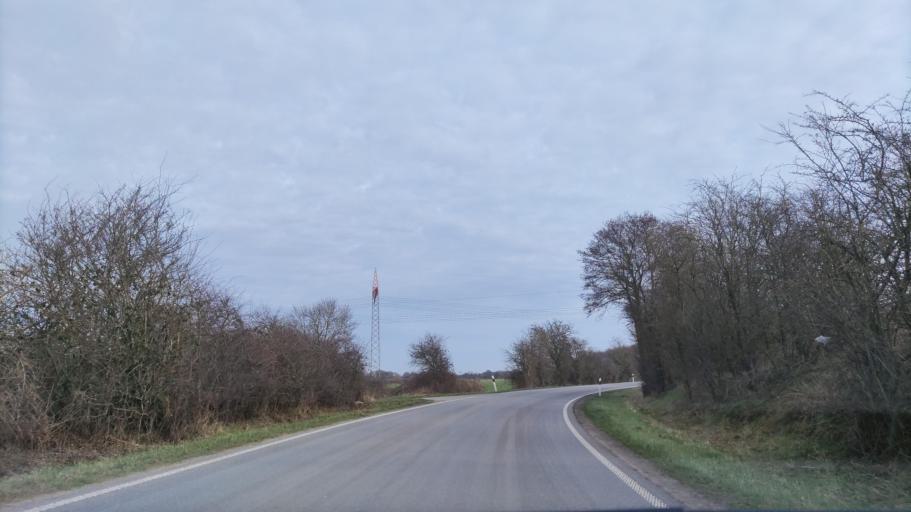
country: DE
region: Schleswig-Holstein
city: Selk
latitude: 54.4779
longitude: 9.5531
